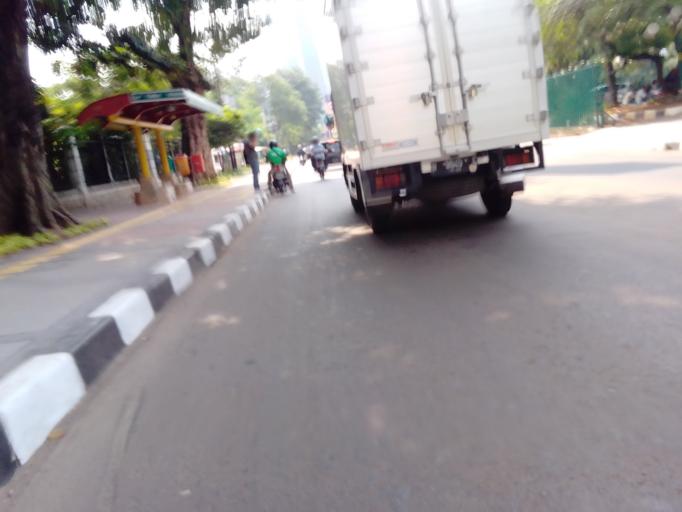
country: ID
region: Jakarta Raya
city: Jakarta
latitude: -6.2133
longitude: 106.7976
